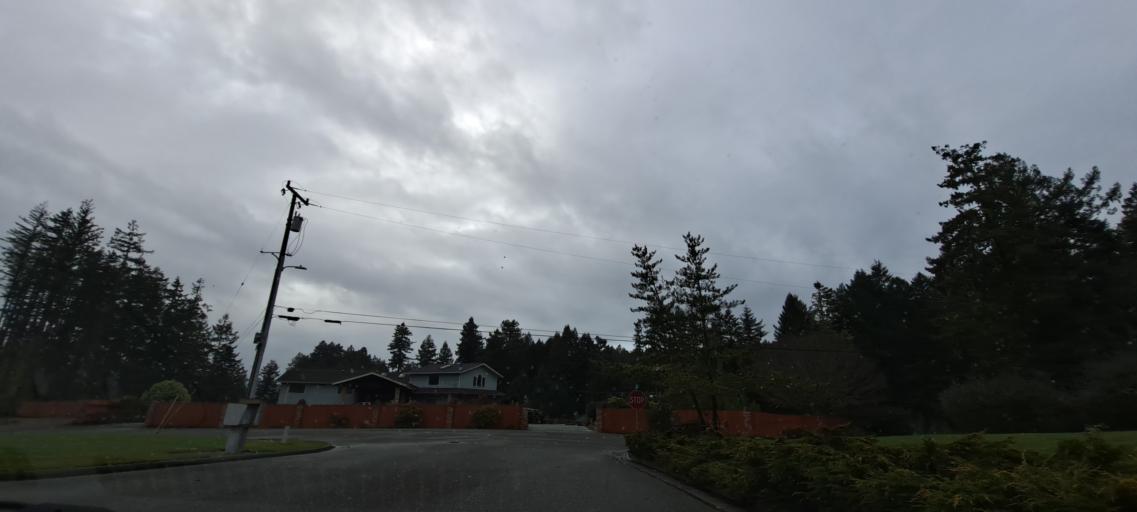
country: US
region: California
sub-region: Humboldt County
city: Fortuna
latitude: 40.6014
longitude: -124.1398
